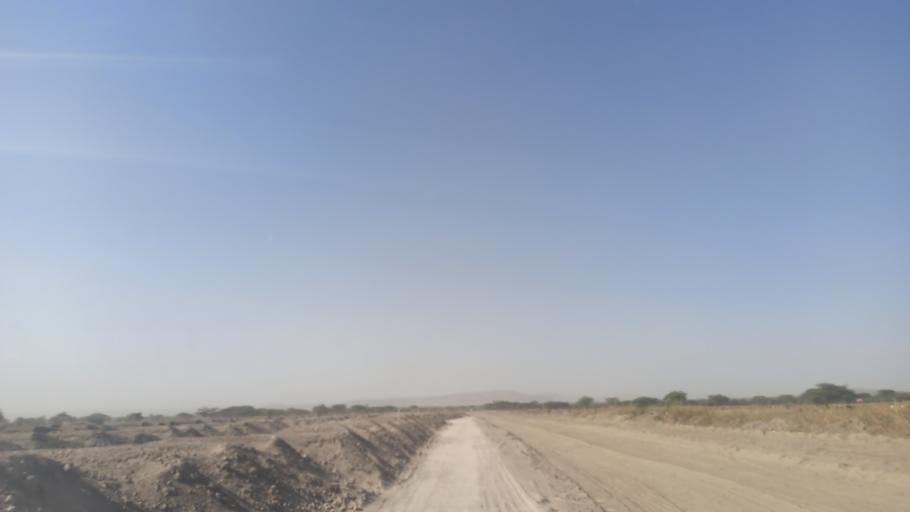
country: ET
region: Oromiya
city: Ziway
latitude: 7.7433
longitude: 38.6187
